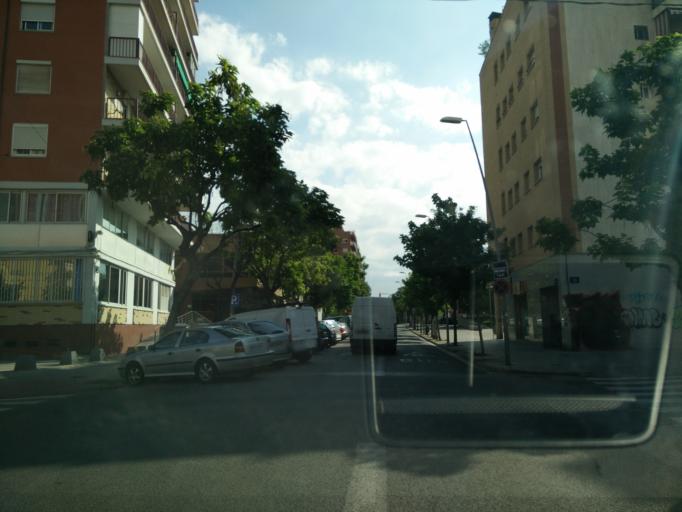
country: ES
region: Catalonia
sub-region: Provincia de Barcelona
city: Badalona
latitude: 41.4438
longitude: 2.2366
